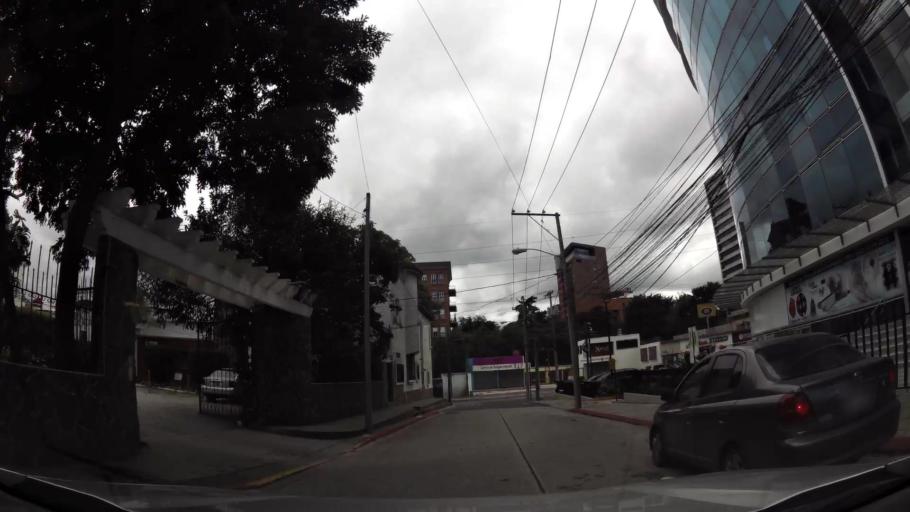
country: GT
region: Guatemala
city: Guatemala City
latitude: 14.6042
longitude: -90.5109
